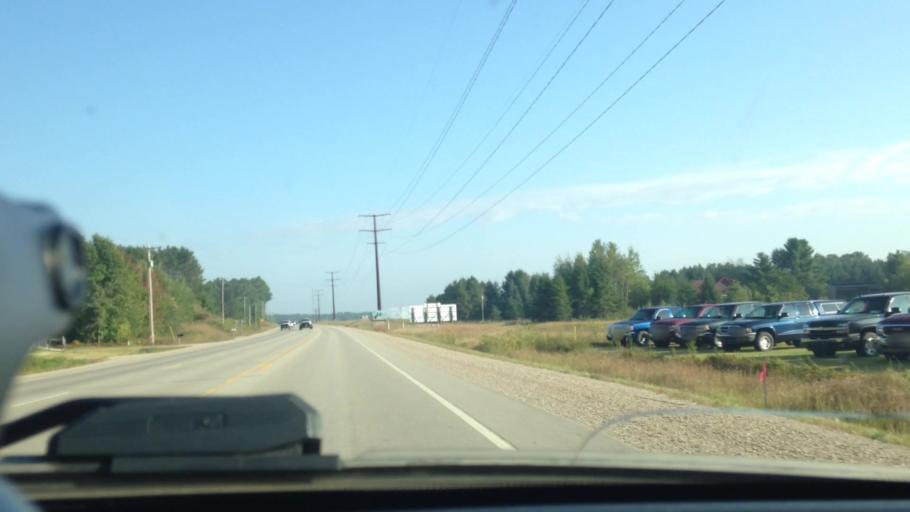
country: US
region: Wisconsin
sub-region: Marinette County
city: Peshtigo
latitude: 45.1962
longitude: -87.9945
